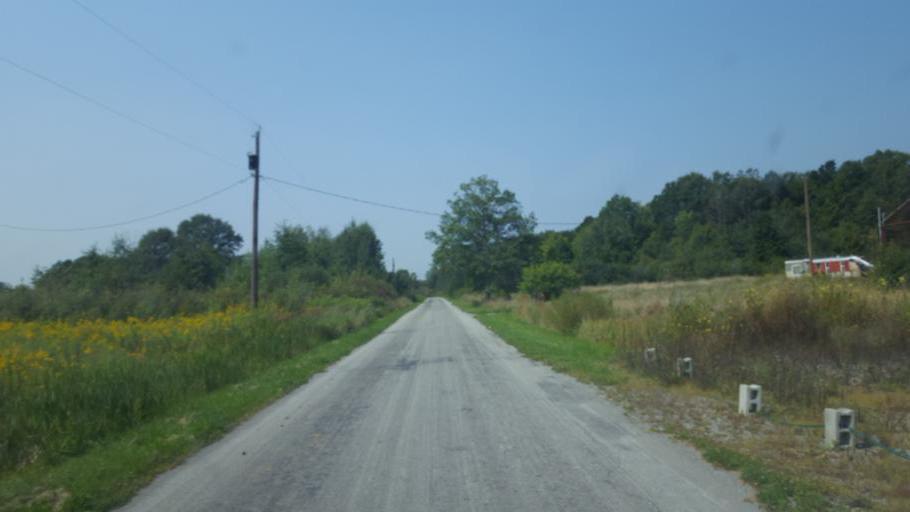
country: US
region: Ohio
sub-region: Ashtabula County
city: Orwell
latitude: 41.4891
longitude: -80.8926
